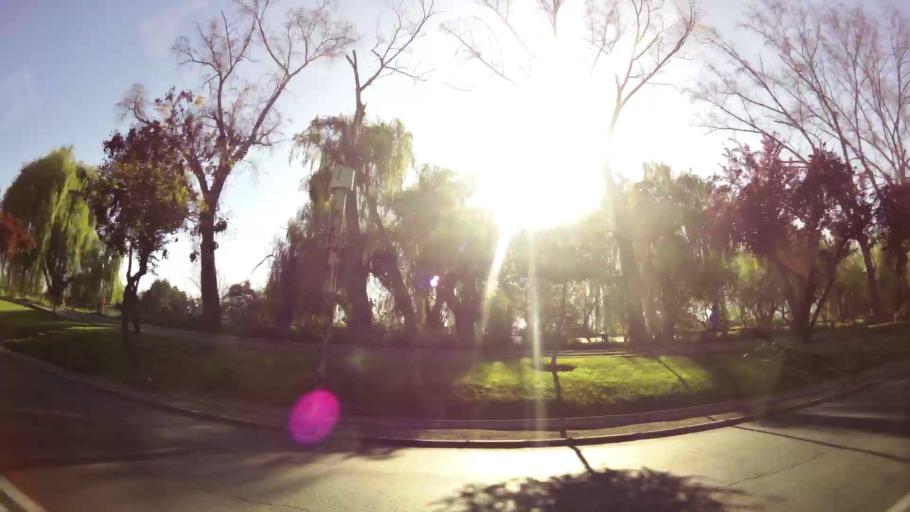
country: CL
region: Santiago Metropolitan
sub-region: Provincia de Santiago
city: Villa Presidente Frei, Nunoa, Santiago, Chile
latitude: -33.4571
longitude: -70.5555
